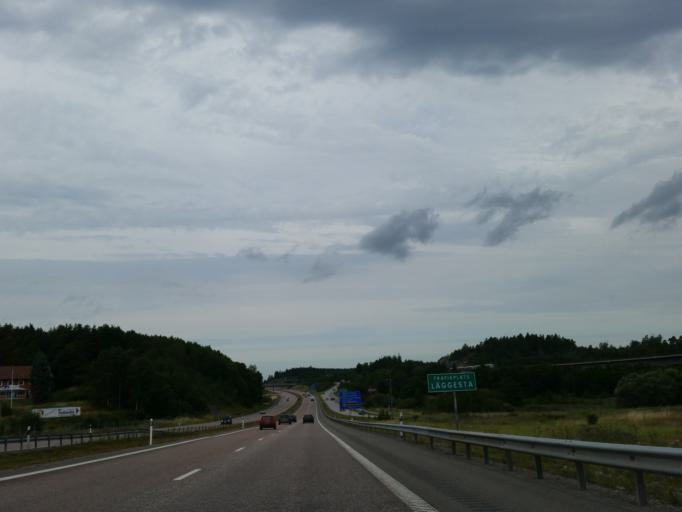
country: SE
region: Soedermanland
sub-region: Strangnas Kommun
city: Mariefred
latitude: 59.2408
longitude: 17.1783
